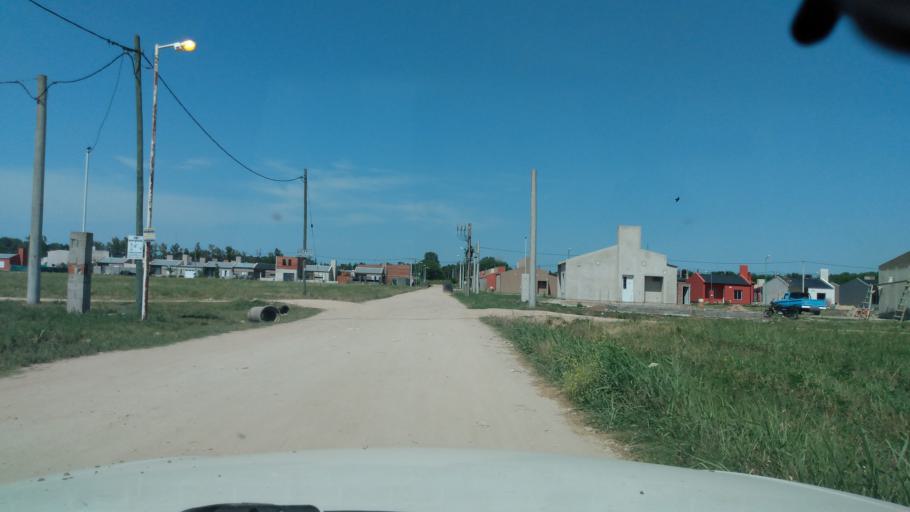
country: AR
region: Buenos Aires
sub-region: Partido de Lujan
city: Lujan
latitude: -34.5529
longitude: -59.1355
